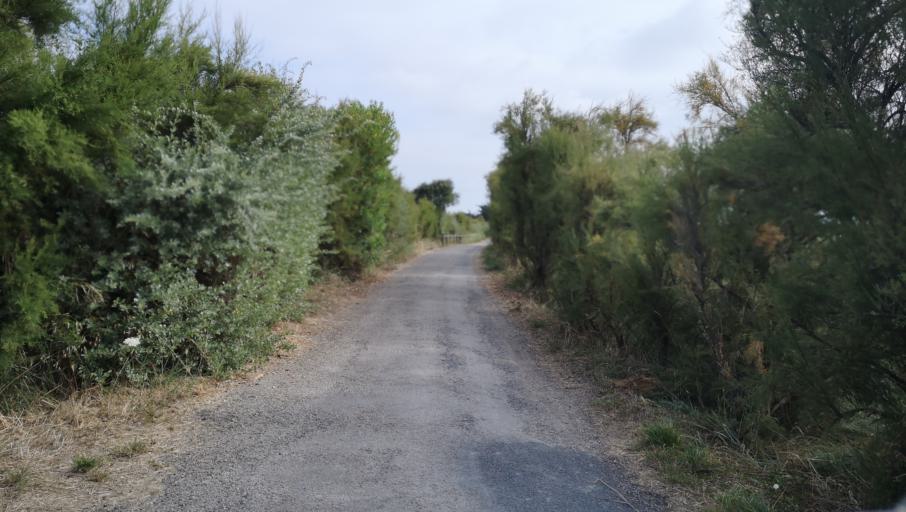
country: FR
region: Pays de la Loire
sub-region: Departement de la Vendee
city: Olonne-sur-Mer
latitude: 46.5346
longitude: -1.8061
